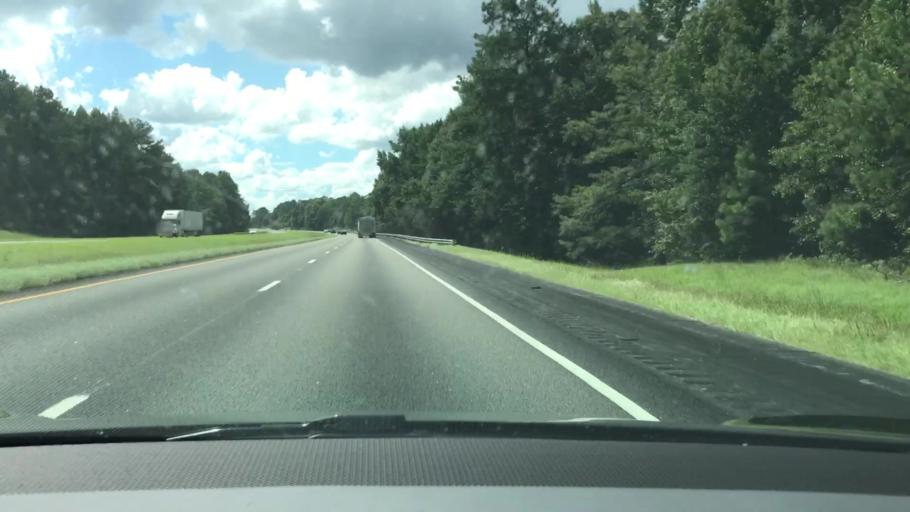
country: US
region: Alabama
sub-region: Elmore County
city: Tallassee
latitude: 32.4364
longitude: -85.8621
